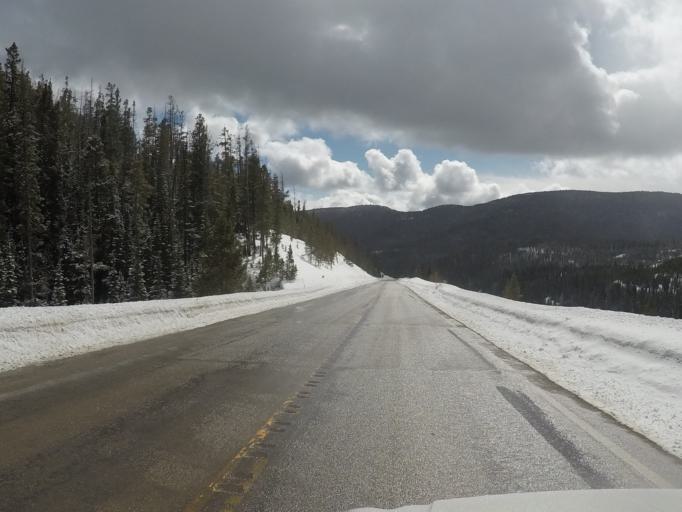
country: US
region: Montana
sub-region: Meagher County
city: White Sulphur Springs
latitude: 46.8222
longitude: -110.6993
